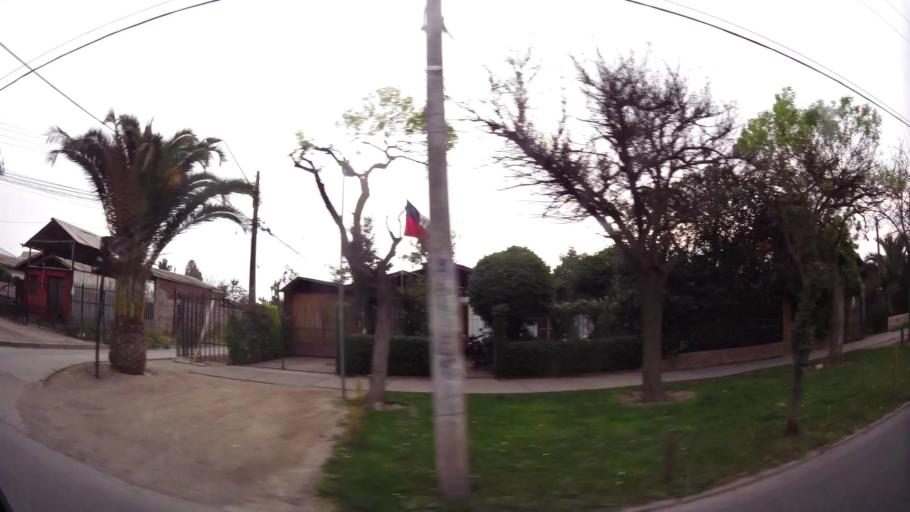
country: CL
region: Santiago Metropolitan
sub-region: Provincia de Santiago
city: Lo Prado
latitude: -33.5136
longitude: -70.7755
